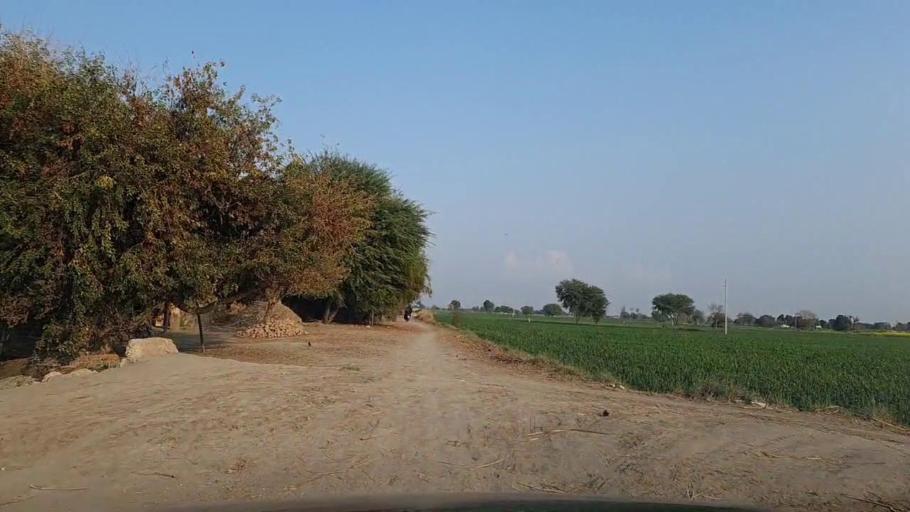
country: PK
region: Sindh
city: Jam Sahib
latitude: 26.3437
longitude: 68.5894
